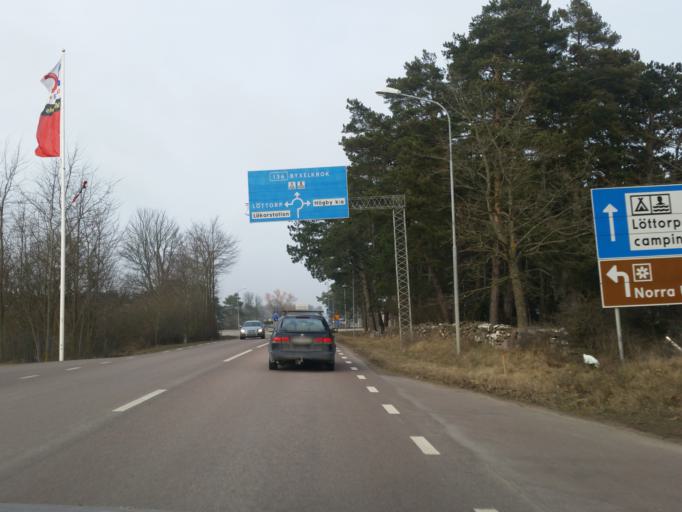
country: SE
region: Kalmar
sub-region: Borgholms Kommun
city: Borgholm
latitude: 57.1634
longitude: 17.0127
